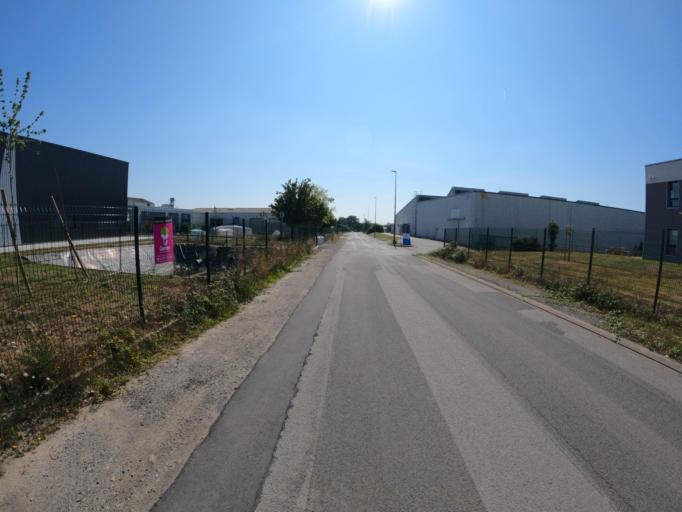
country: FR
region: Pays de la Loire
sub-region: Departement de la Loire-Atlantique
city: Pont-Saint-Martin
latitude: 47.1527
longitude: -1.5887
